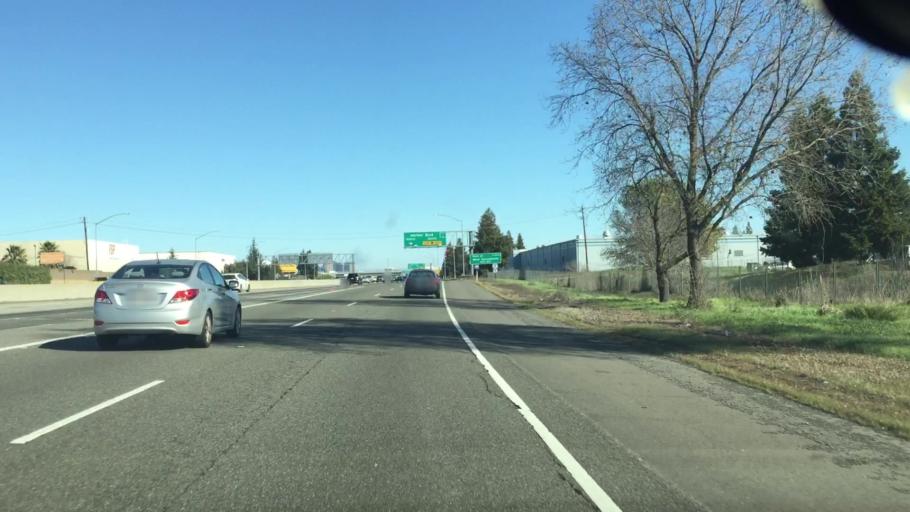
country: US
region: California
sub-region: Yolo County
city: West Sacramento
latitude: 38.5749
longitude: -121.5575
